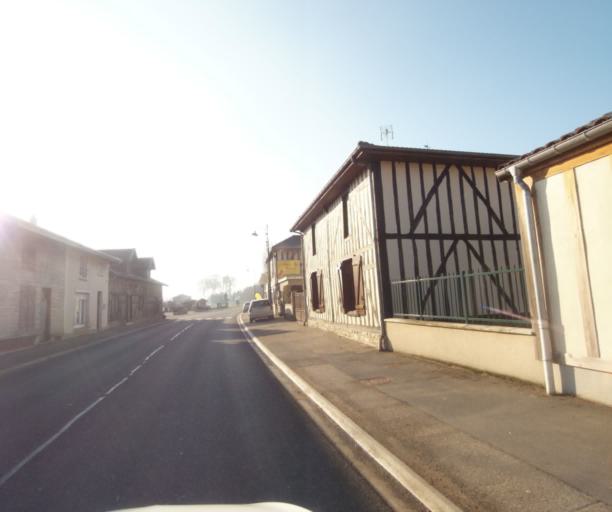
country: FR
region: Champagne-Ardenne
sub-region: Departement de la Haute-Marne
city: Montier-en-Der
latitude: 48.4704
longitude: 4.7640
